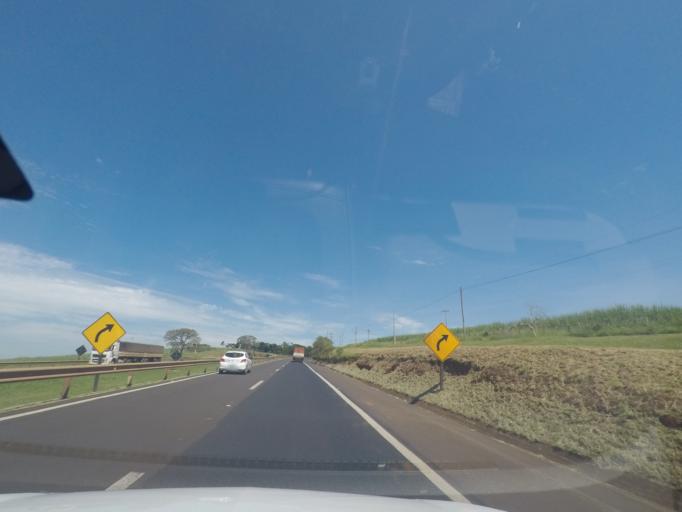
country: BR
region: Sao Paulo
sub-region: Araraquara
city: Araraquara
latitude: -21.8762
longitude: -48.0953
